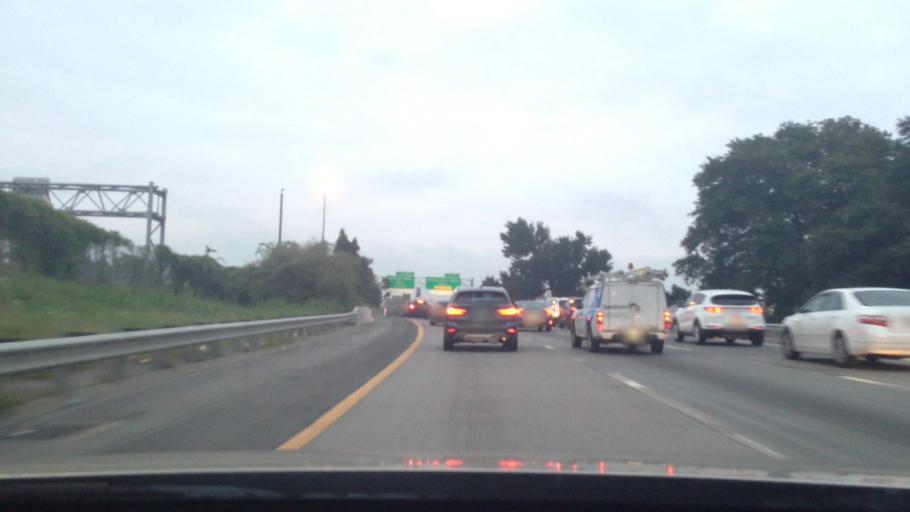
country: US
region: New York
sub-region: Bronx
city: Eastchester
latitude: 40.8617
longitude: -73.8292
